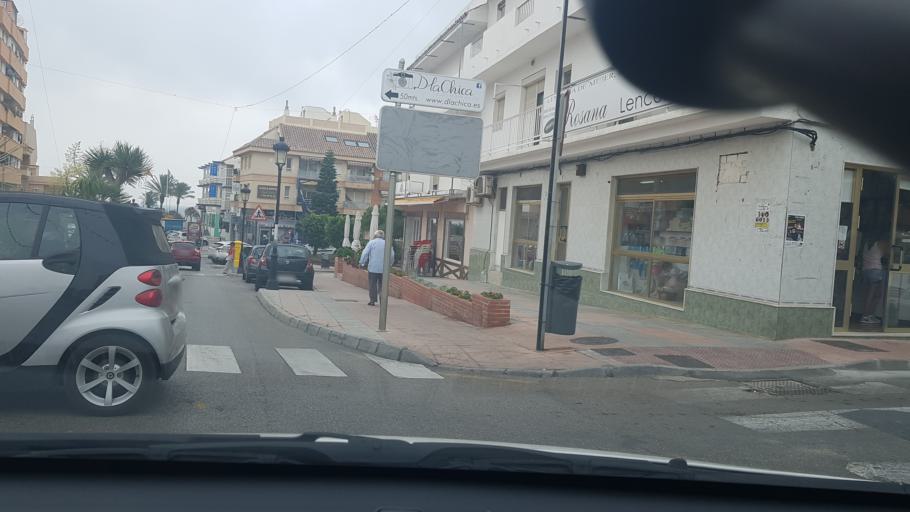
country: ES
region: Andalusia
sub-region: Provincia de Malaga
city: Manilva
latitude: 36.3666
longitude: -5.2269
